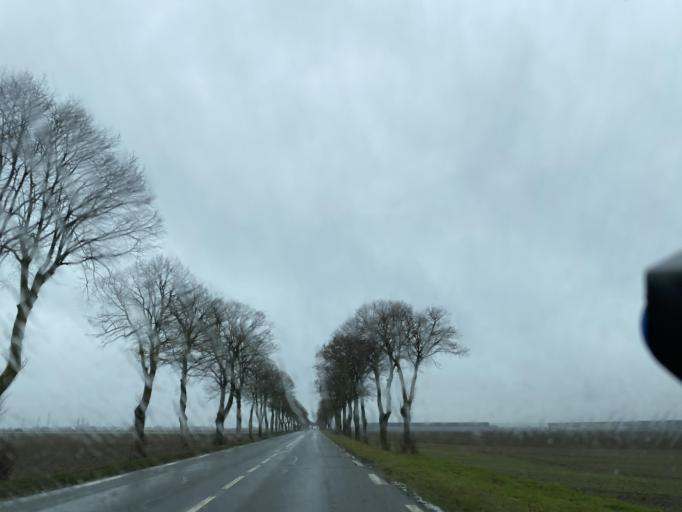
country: FR
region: Centre
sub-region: Departement du Loiret
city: Artenay
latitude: 48.1031
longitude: 1.8645
